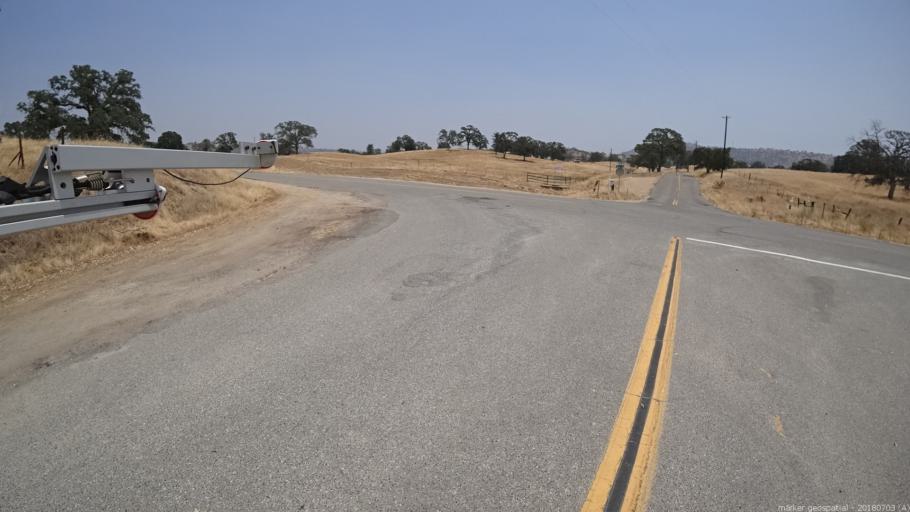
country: US
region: California
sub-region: Madera County
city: Yosemite Lakes
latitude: 37.0566
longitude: -119.7144
